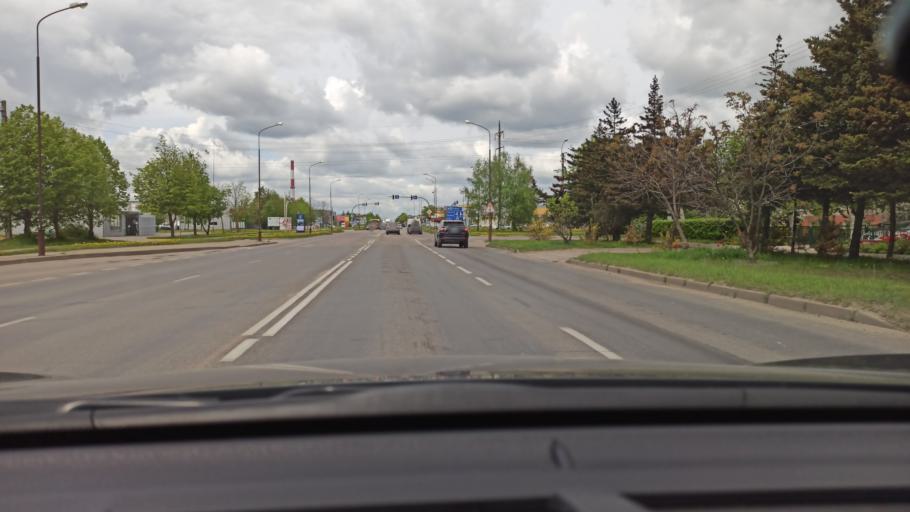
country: LT
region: Siauliu apskritis
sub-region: Siauliai
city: Siauliai
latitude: 55.9047
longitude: 23.3295
